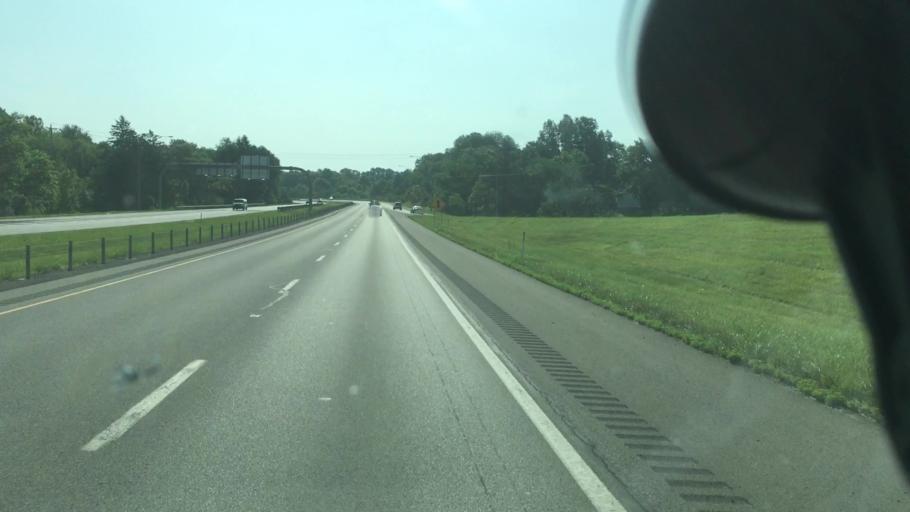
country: US
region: Pennsylvania
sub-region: Lawrence County
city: New Castle
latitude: 40.9721
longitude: -80.3123
